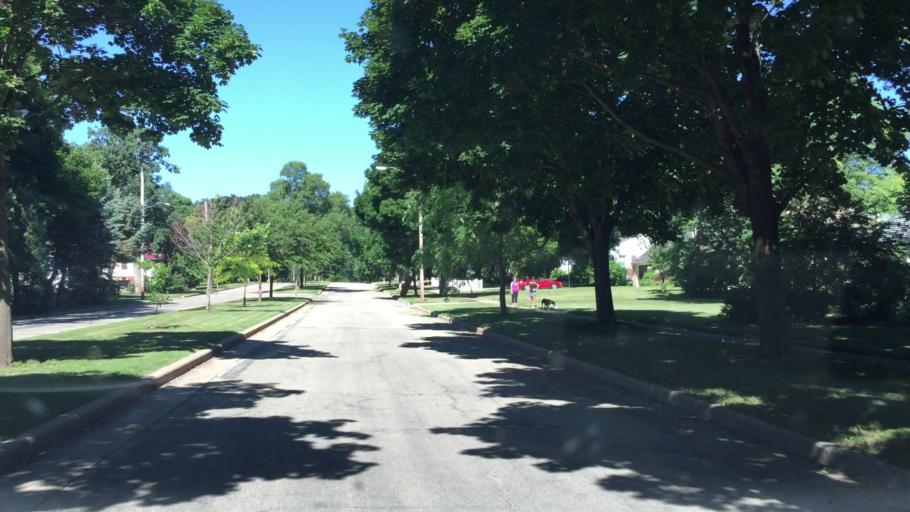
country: US
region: Wisconsin
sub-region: Winnebago County
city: Menasha
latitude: 44.1936
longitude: -88.4373
